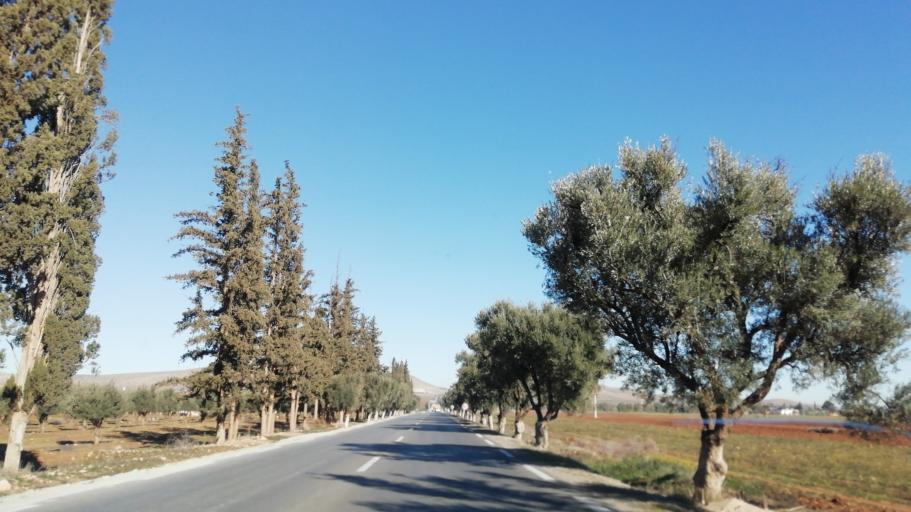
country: DZ
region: Mascara
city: Mascara
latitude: 35.2132
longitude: 0.1114
